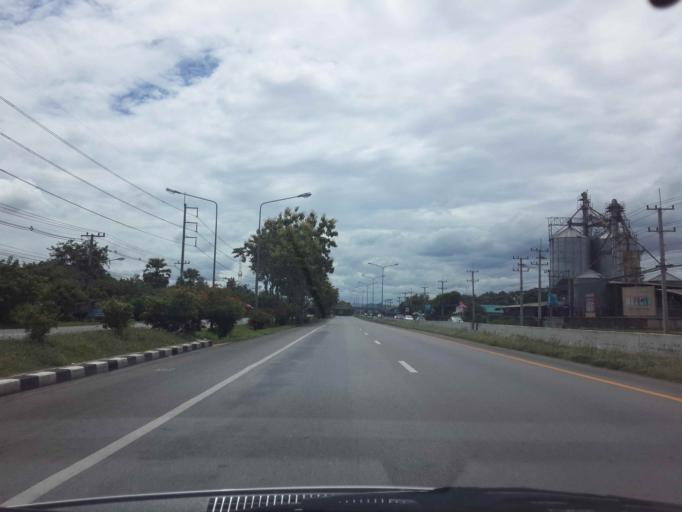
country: TH
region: Phetchaburi
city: Phetchaburi
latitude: 13.1176
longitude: 99.9081
